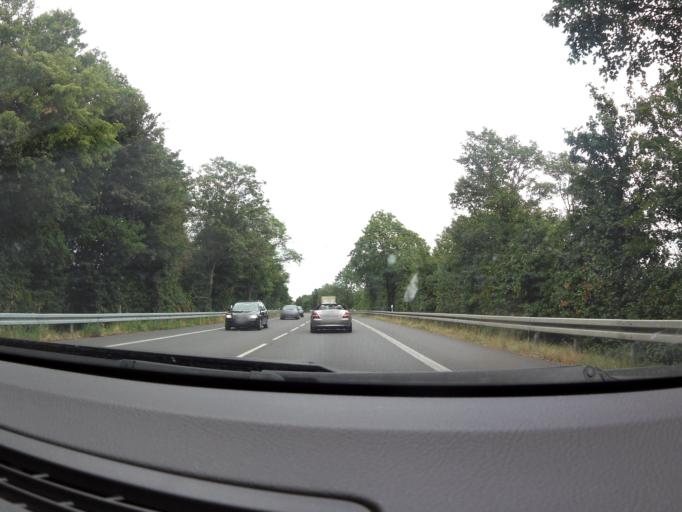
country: DE
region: North Rhine-Westphalia
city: Straelen
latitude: 51.4333
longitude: 6.2776
